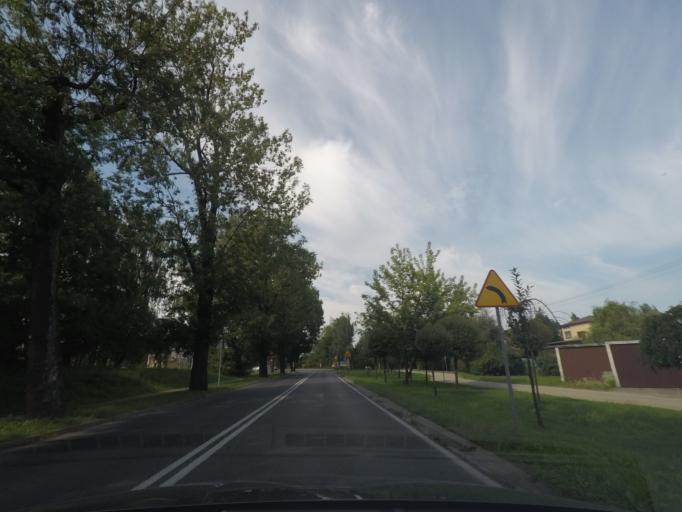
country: PL
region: Lesser Poland Voivodeship
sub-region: Powiat oswiecimski
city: Brzeszcze
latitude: 49.9735
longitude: 19.1293
